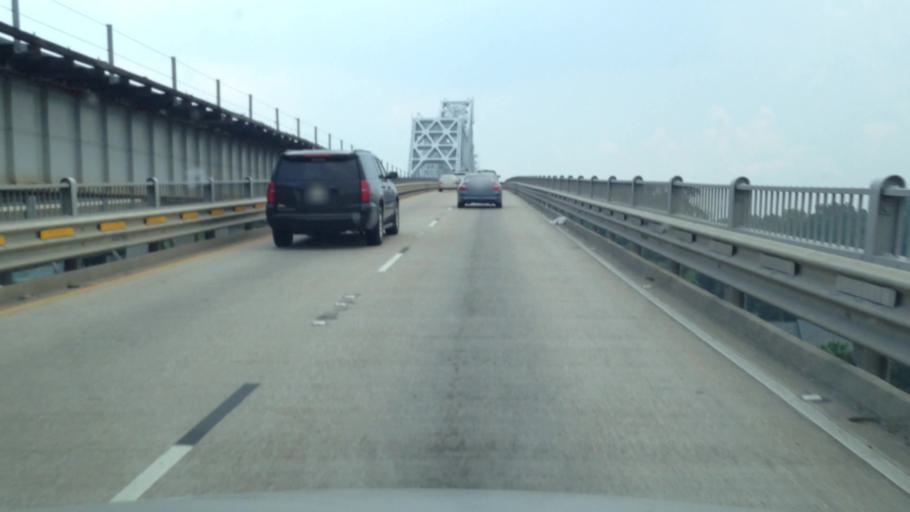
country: US
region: Louisiana
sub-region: West Baton Rouge Parish
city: Port Allen
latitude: 30.5064
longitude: -91.2054
